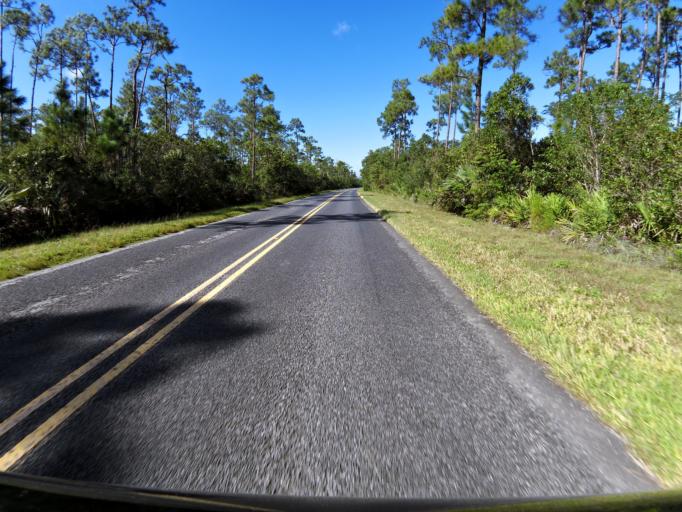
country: US
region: Florida
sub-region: Miami-Dade County
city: Florida City
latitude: 25.4242
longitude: -80.6819
